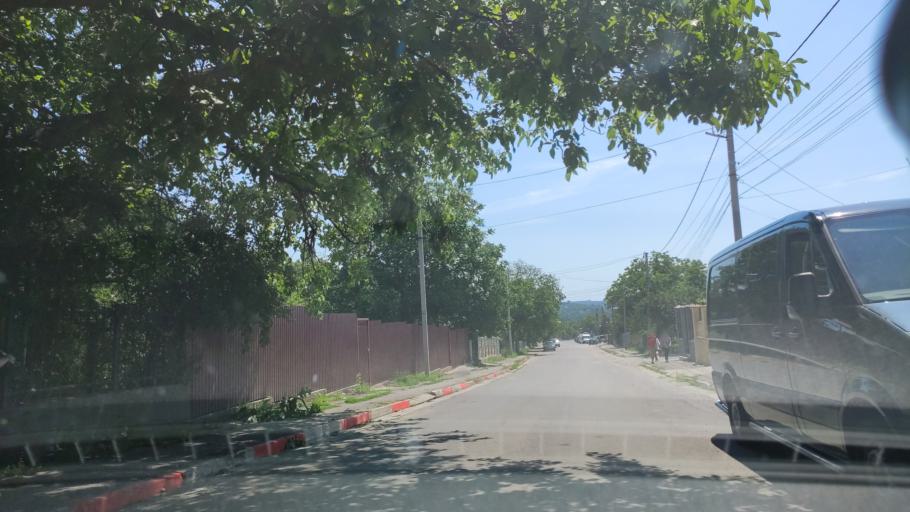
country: MD
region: Raionul Soroca
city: Soroca
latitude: 48.1681
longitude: 28.3013
